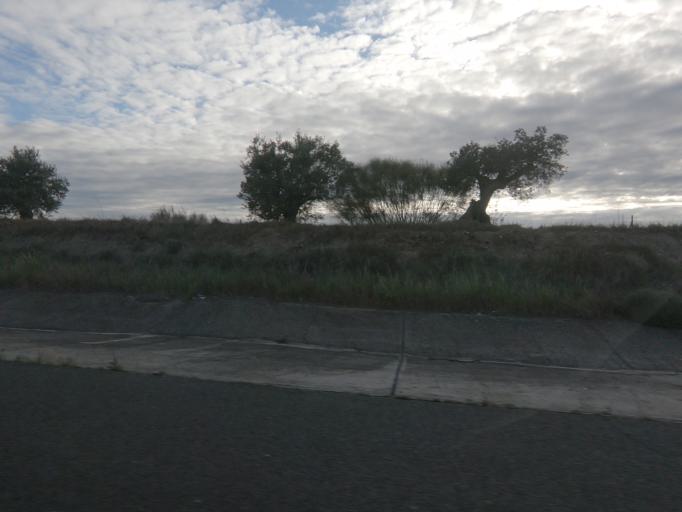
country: ES
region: Extremadura
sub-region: Provincia de Caceres
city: Santiago del Campo
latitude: 39.6646
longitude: -6.3936
